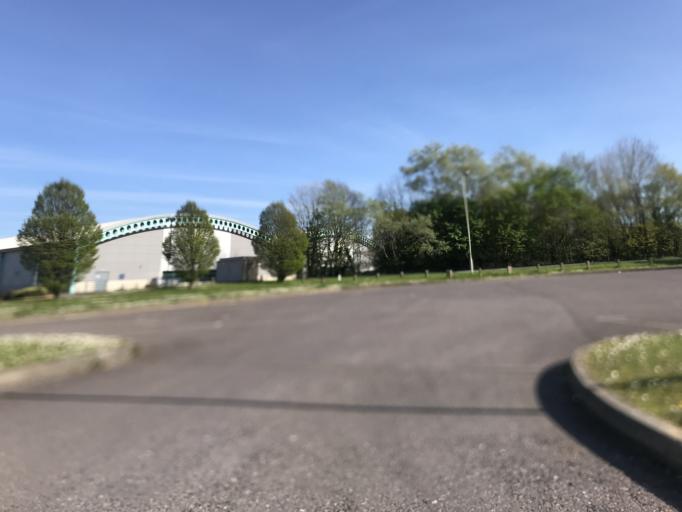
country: GB
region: England
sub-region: Devon
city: Barnstaple
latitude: 51.0725
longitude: -4.0590
